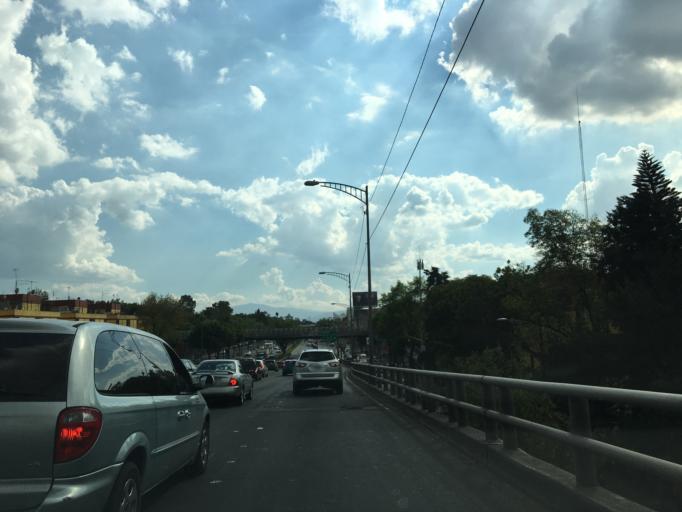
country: MX
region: Mexico City
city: Mexico City
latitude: 19.4255
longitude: -99.1116
